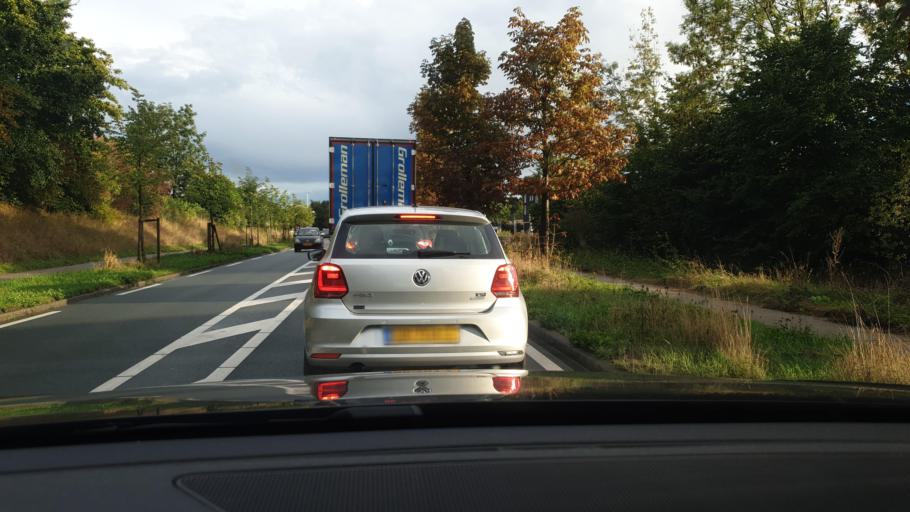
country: NL
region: North Brabant
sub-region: Gemeente Landerd
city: Schaijk
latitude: 51.7957
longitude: 5.6445
